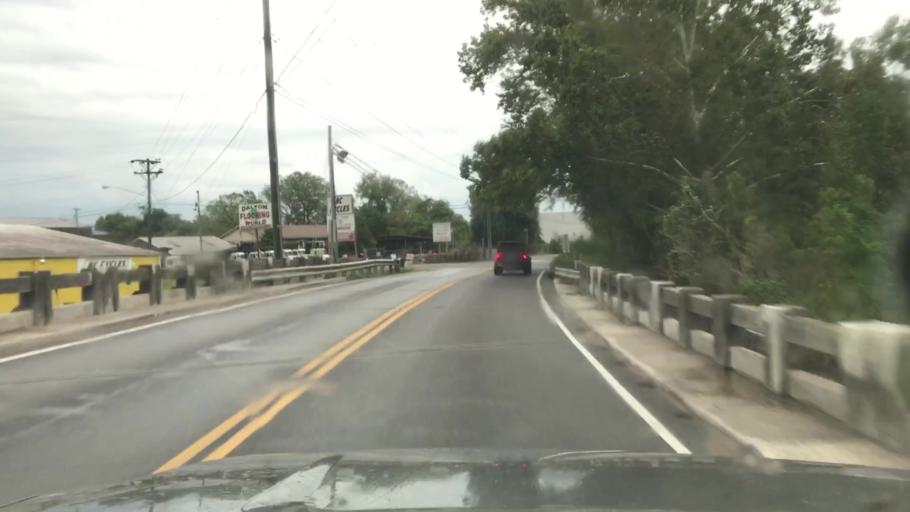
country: US
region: Tennessee
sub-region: Davidson County
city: Lakewood
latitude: 36.1852
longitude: -86.6261
